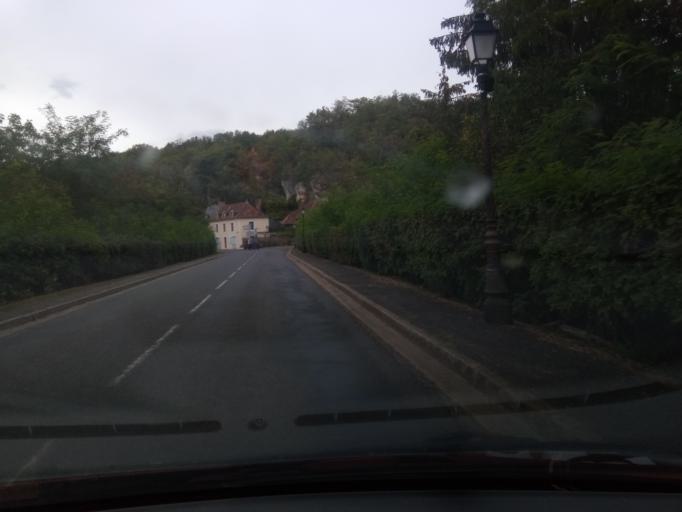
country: FR
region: Poitou-Charentes
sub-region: Departement de la Vienne
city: Pleumartin
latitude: 46.6805
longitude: 0.8388
